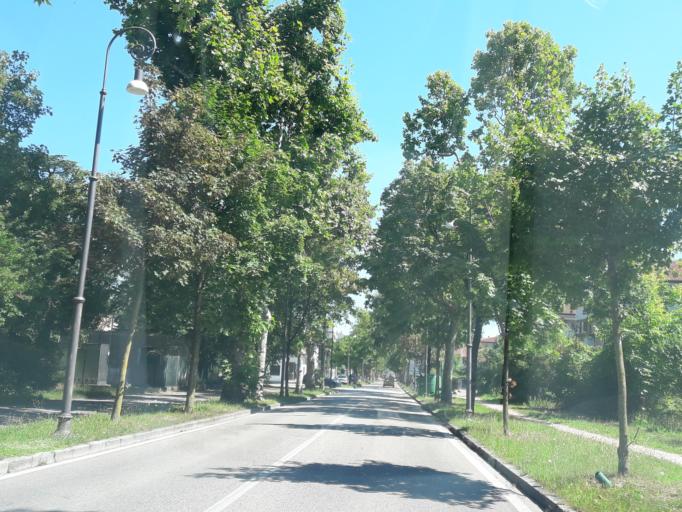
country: IT
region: Friuli Venezia Giulia
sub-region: Provincia di Udine
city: Udine
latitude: 46.0597
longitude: 13.2191
